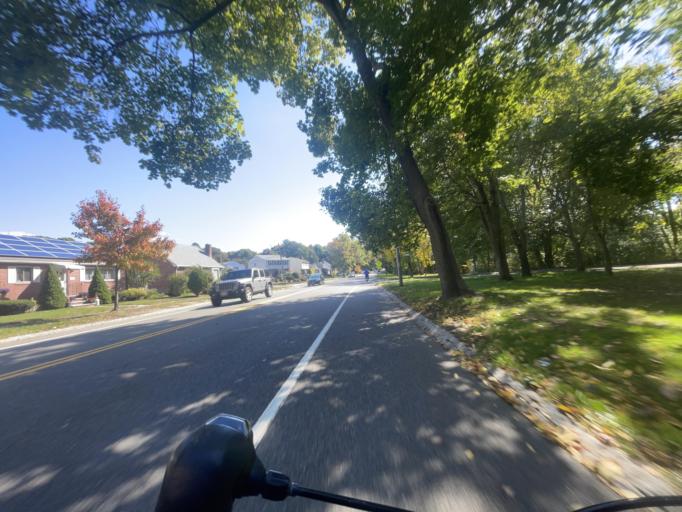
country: US
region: Massachusetts
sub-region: Norfolk County
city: Quincy
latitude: 42.2479
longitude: -71.0277
